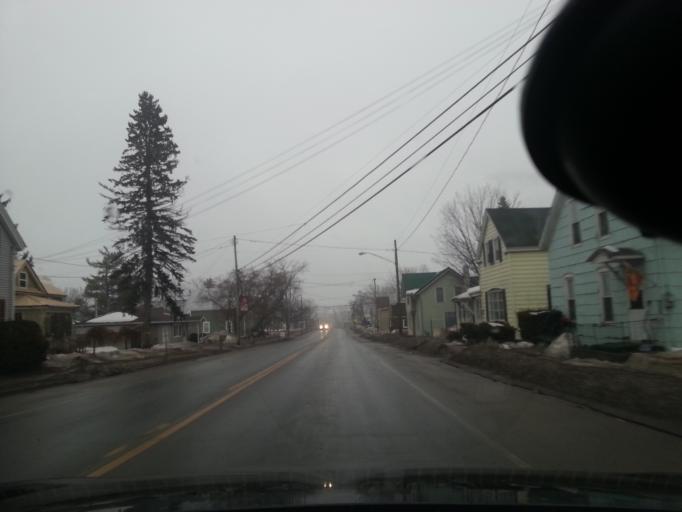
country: US
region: New York
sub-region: St. Lawrence County
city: Ogdensburg
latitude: 44.6197
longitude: -75.4100
